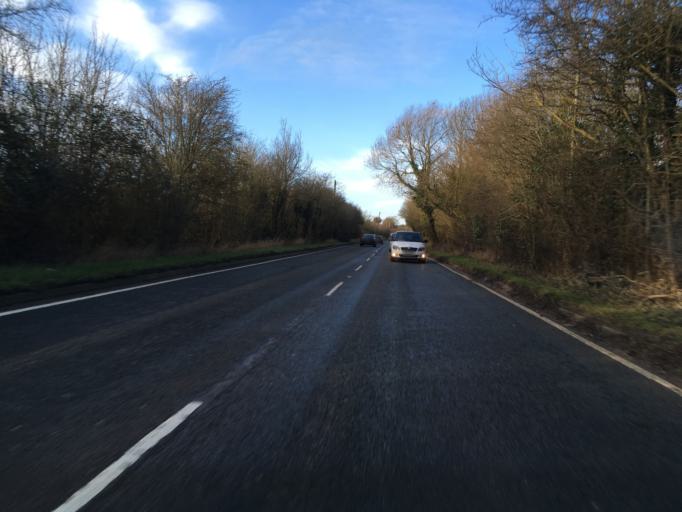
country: GB
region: England
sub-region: Warwickshire
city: Stratford-upon-Avon
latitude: 52.2134
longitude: -1.7265
